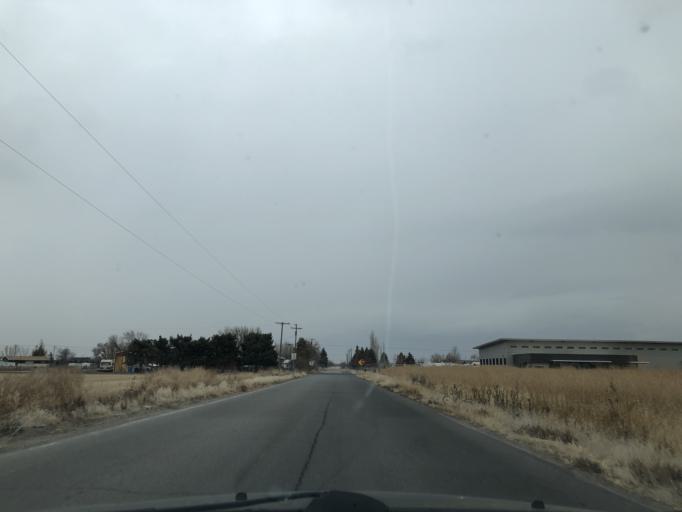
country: US
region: Utah
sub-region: Cache County
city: Nibley
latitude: 41.6918
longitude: -111.8622
